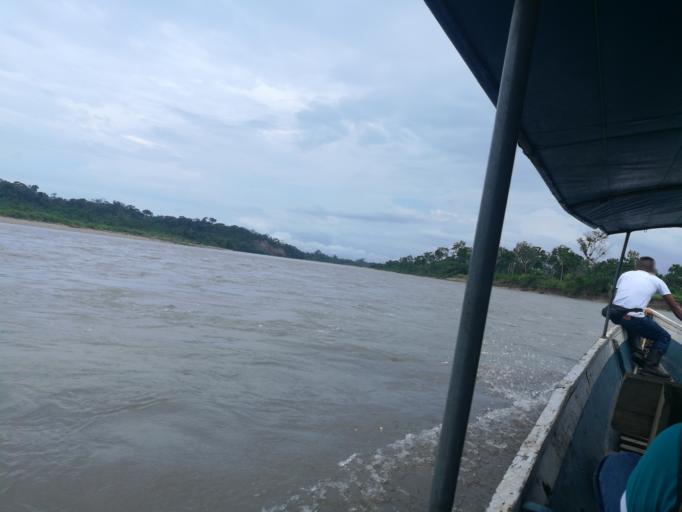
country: EC
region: Orellana
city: Boca Suno
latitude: -0.7701
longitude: -77.1792
